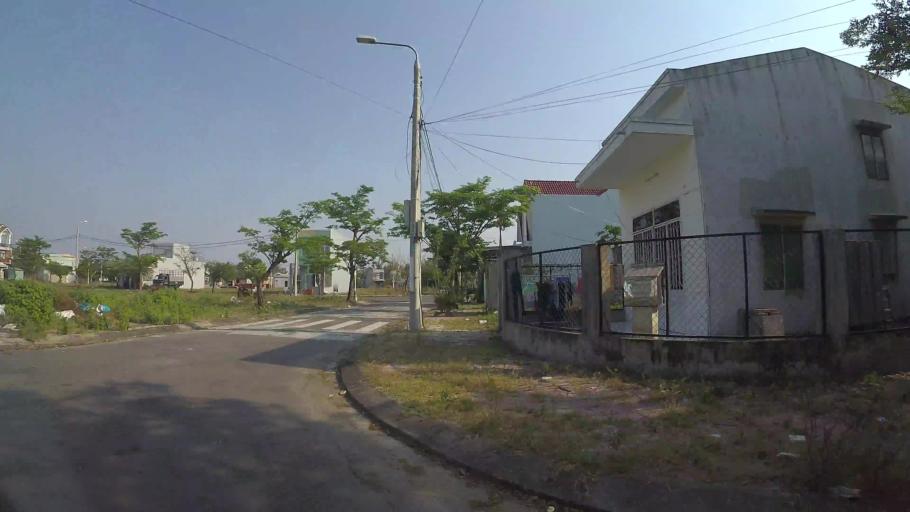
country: VN
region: Quang Nam
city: Quang Nam
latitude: 15.9472
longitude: 108.2582
